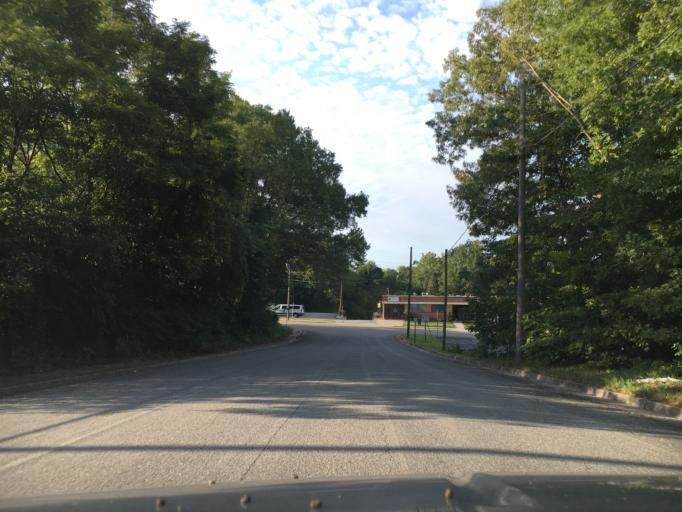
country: US
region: Virginia
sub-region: Halifax County
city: South Boston
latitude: 36.6977
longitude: -78.8927
